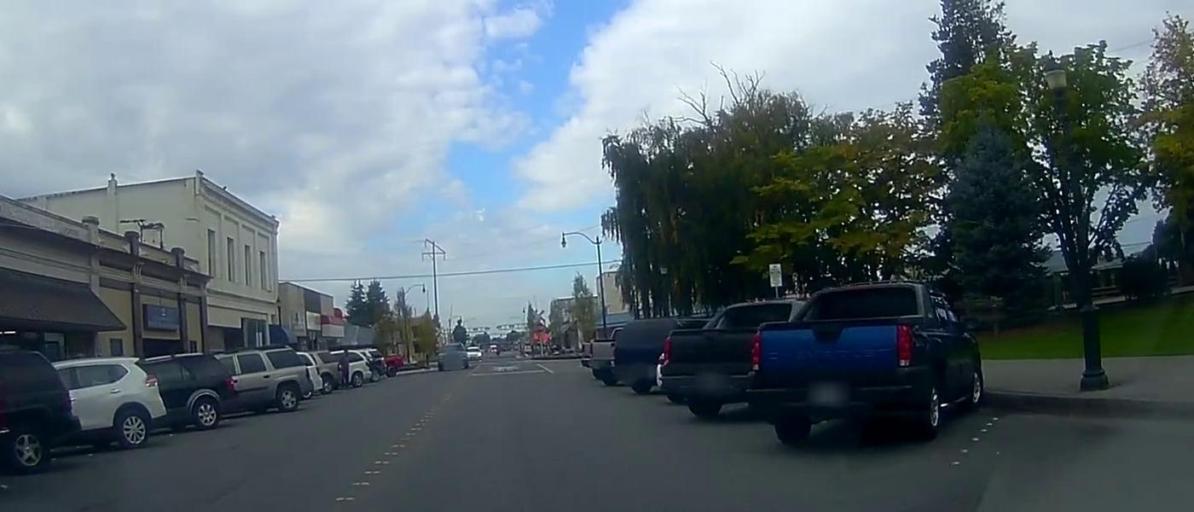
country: US
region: Washington
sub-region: Skagit County
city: Burlington
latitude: 48.4756
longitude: -122.3268
